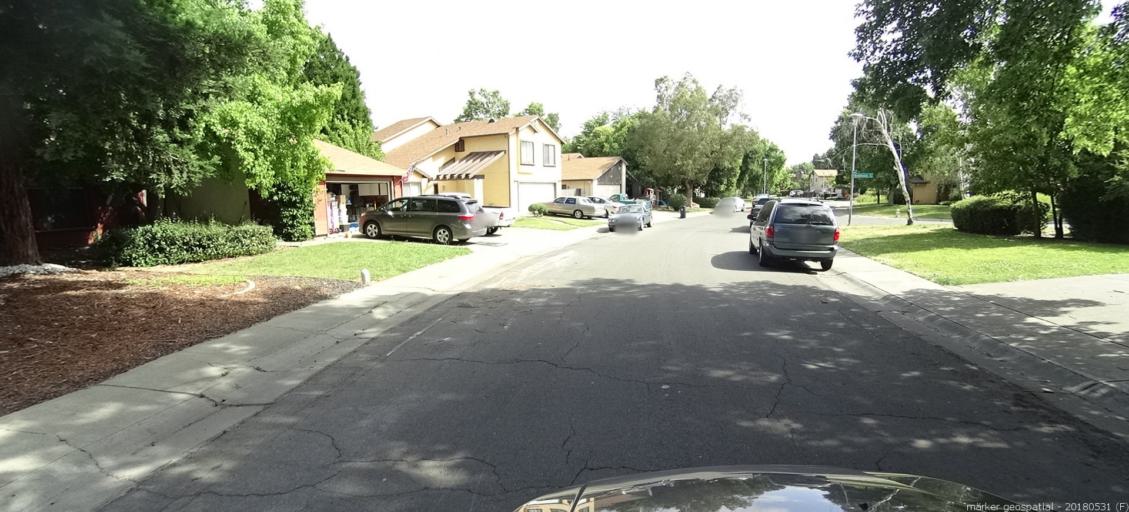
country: US
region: California
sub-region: Sacramento County
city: Sacramento
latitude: 38.6212
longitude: -121.4904
